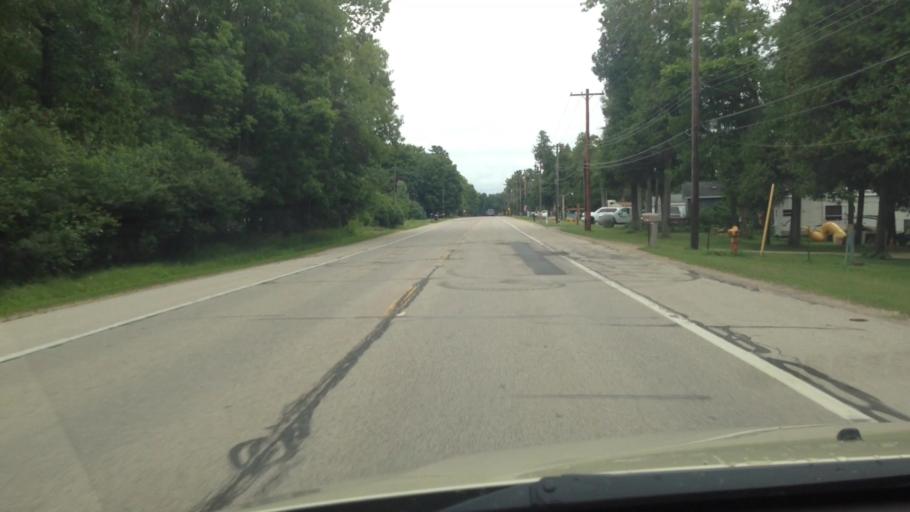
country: US
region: Michigan
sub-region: Delta County
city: Escanaba
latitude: 45.6865
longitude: -87.1137
